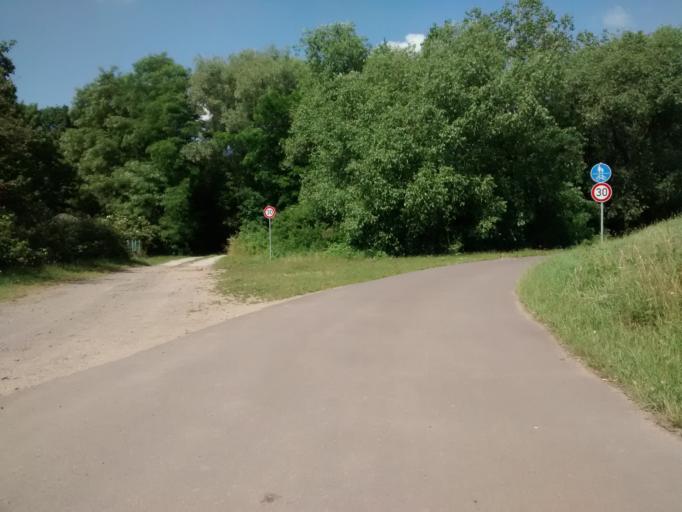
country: DE
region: Saxony-Anhalt
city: Wittenburg
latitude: 51.8471
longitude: 12.5903
